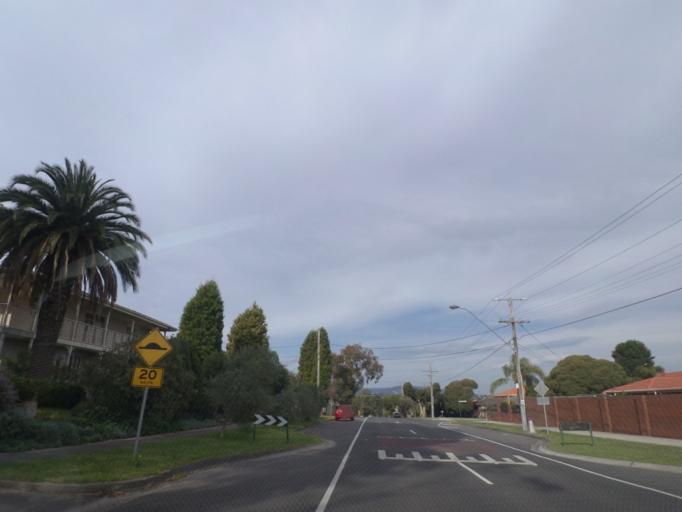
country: AU
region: Victoria
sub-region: Whitehorse
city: Vermont
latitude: -37.8507
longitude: 145.1995
